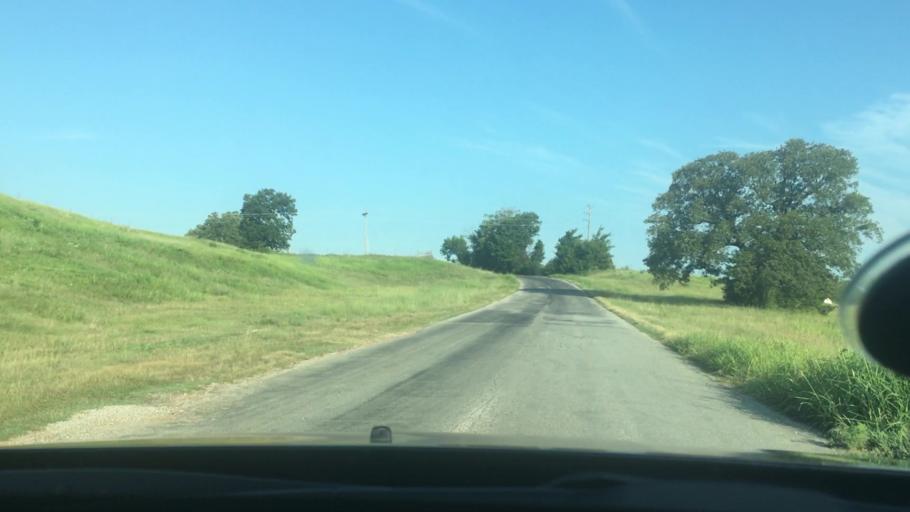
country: US
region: Oklahoma
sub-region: Pontotoc County
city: Ada
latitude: 34.7813
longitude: -96.7168
